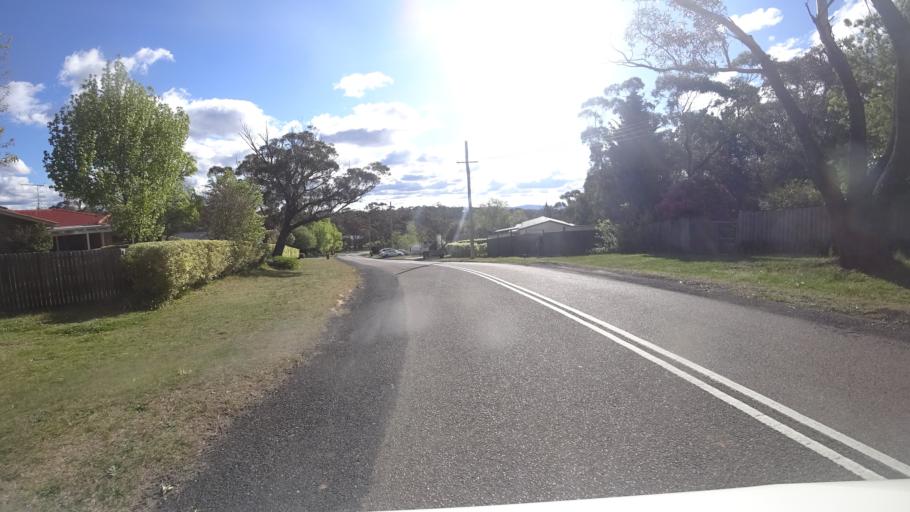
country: AU
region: New South Wales
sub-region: Blue Mountains Municipality
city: Katoomba
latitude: -33.7204
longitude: 150.2935
